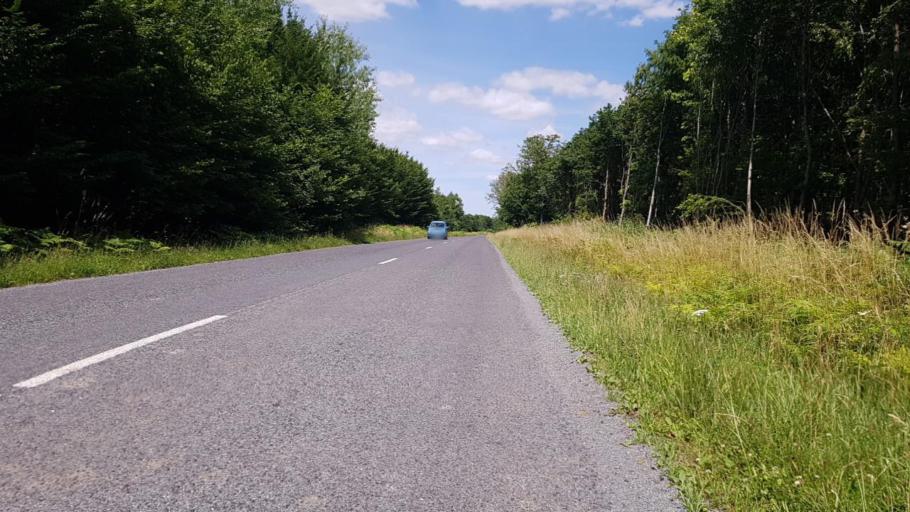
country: FR
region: Picardie
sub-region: Departement de l'Oise
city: Carlepont
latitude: 49.5201
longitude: 2.9834
